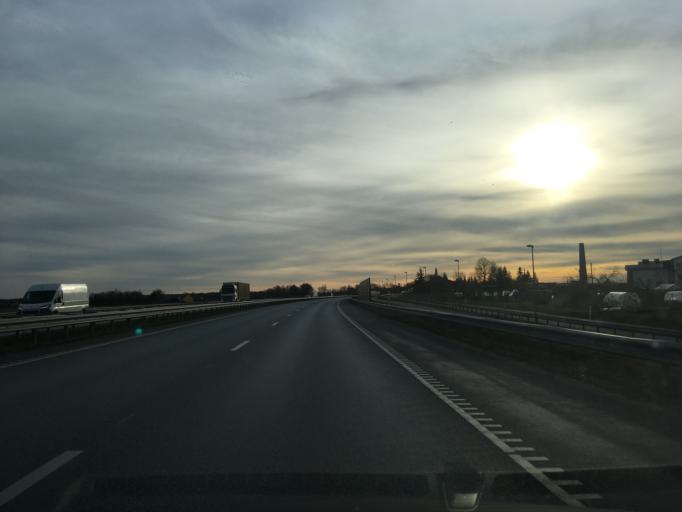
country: EE
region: Ida-Virumaa
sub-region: Johvi vald
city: Johvi
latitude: 59.3801
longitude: 27.3703
